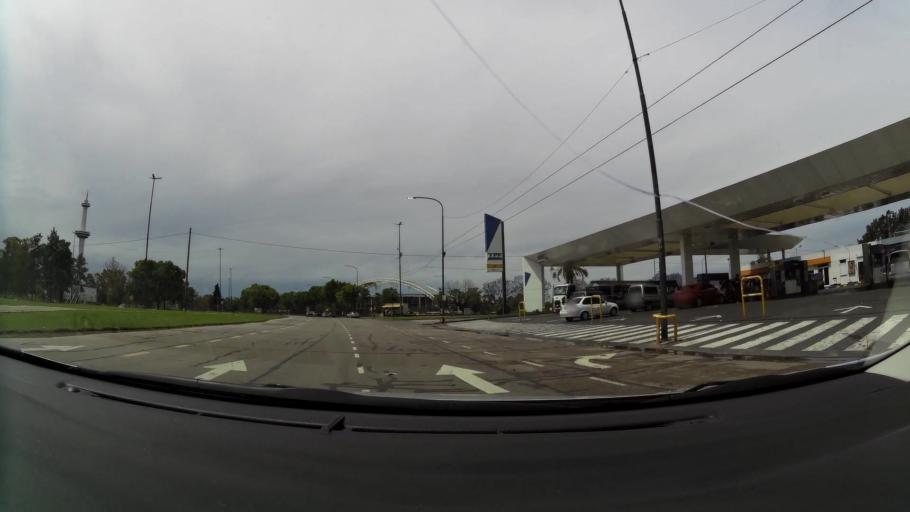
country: AR
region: Buenos Aires F.D.
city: Villa Lugano
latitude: -34.6808
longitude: -58.4506
